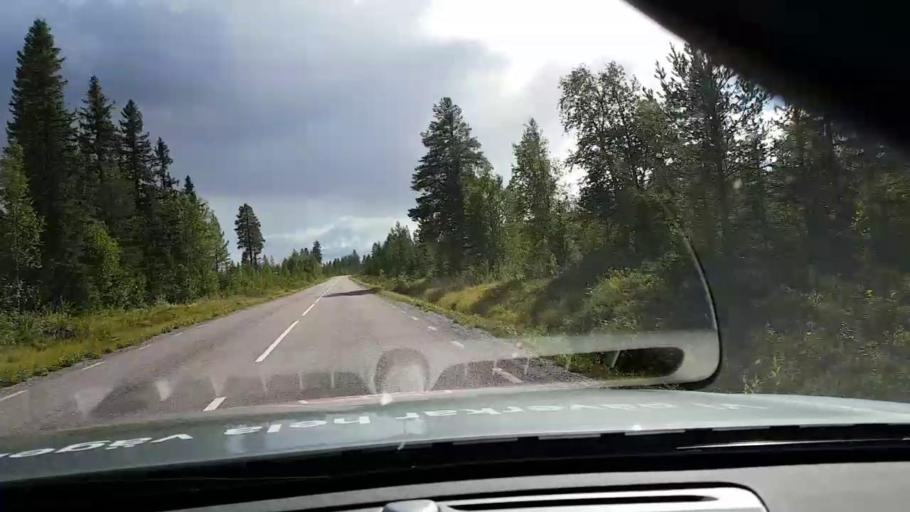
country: SE
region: Vaesterbotten
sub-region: Asele Kommun
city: Asele
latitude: 63.8949
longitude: 17.3500
